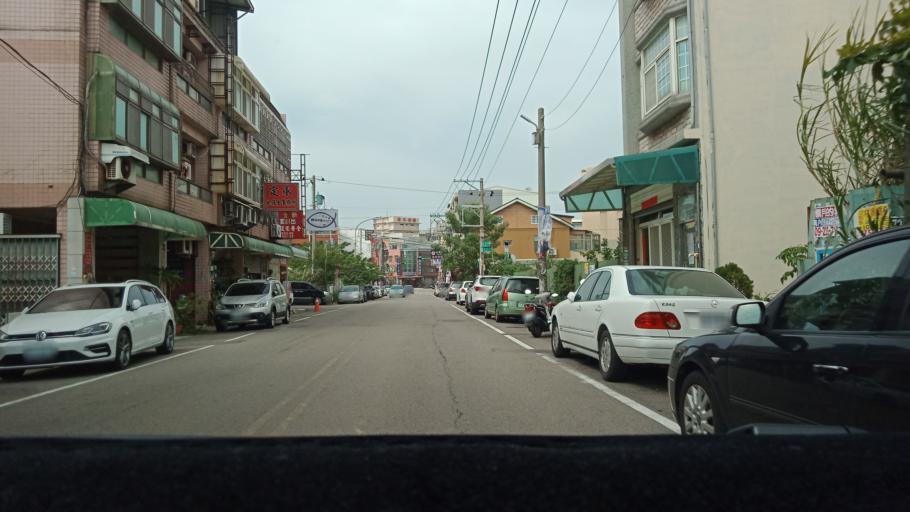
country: TW
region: Taiwan
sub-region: Hsinchu
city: Zhubei
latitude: 24.8748
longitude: 120.9969
